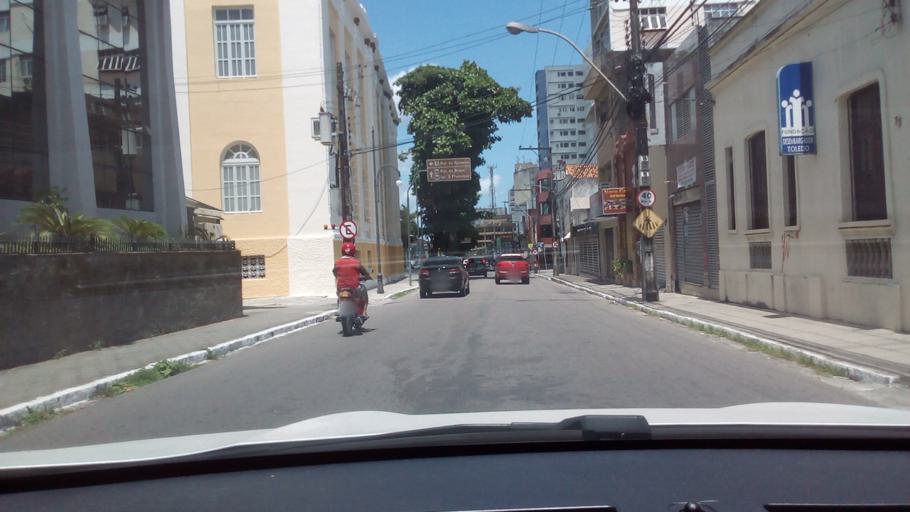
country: BR
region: Paraiba
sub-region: Joao Pessoa
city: Joao Pessoa
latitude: -7.1228
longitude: -34.8836
